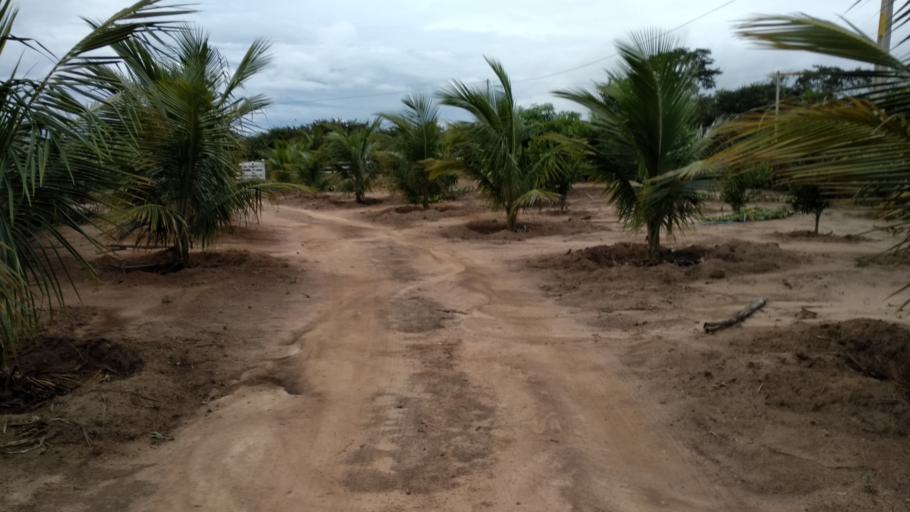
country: BR
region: Bahia
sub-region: Caetite
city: Caetite
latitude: -13.9767
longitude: -42.5174
